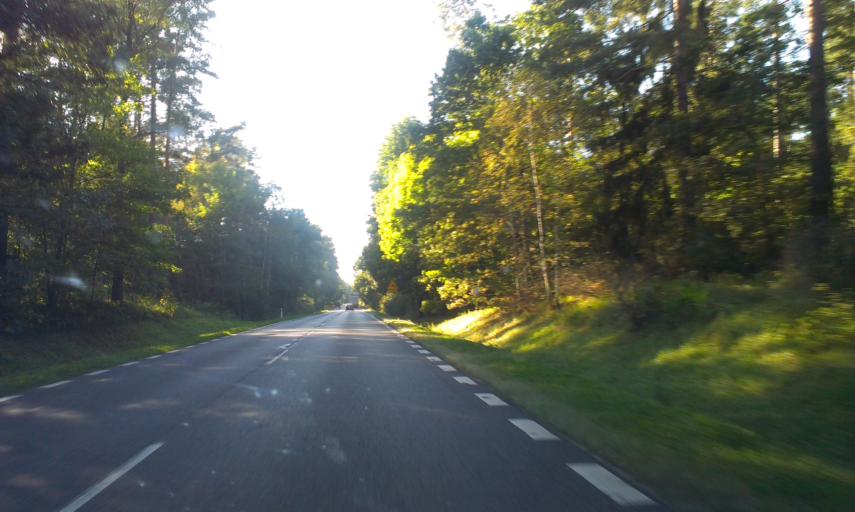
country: PL
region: Kujawsko-Pomorskie
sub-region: Powiat swiecki
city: Swiekatowo
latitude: 53.4883
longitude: 18.1079
